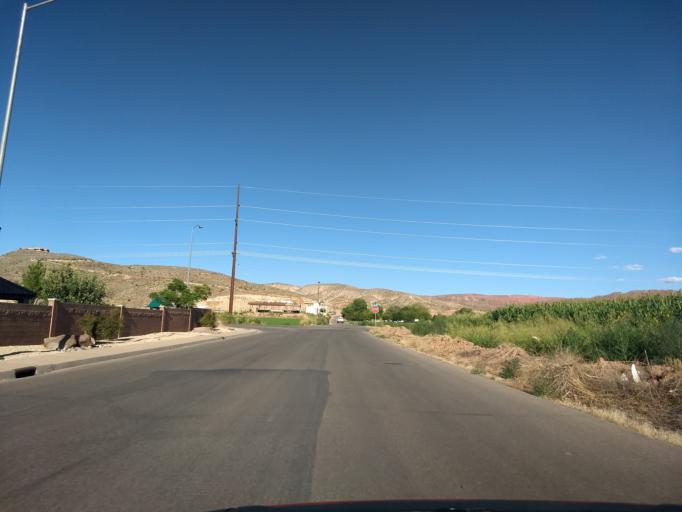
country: US
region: Utah
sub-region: Washington County
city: Washington
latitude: 37.0959
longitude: -113.5099
